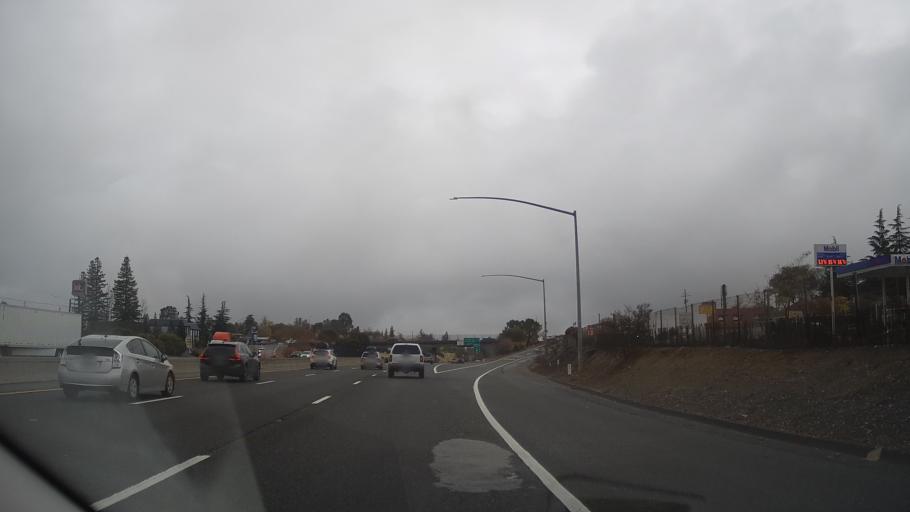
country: US
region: California
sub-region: Placer County
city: North Auburn
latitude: 38.9261
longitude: -121.0567
